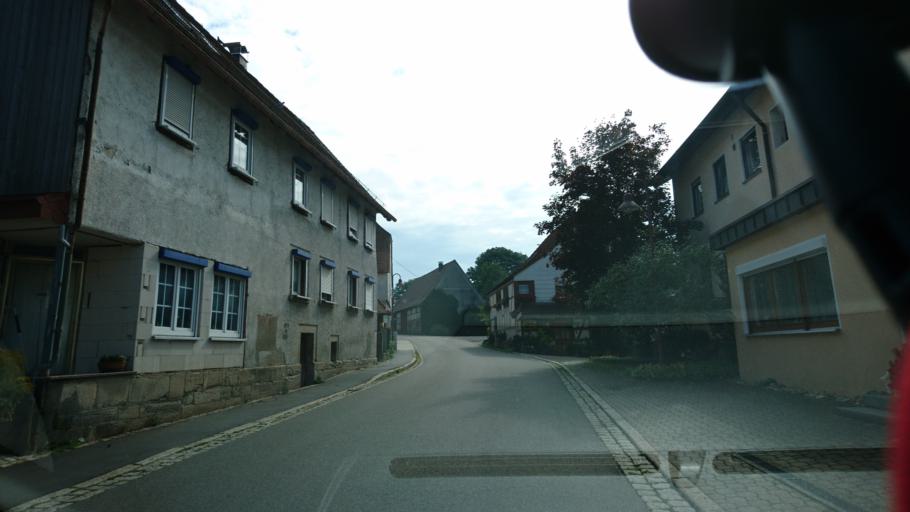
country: DE
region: Baden-Wuerttemberg
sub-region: Regierungsbezirk Stuttgart
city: Mainhardt
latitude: 49.1030
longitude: 9.5682
